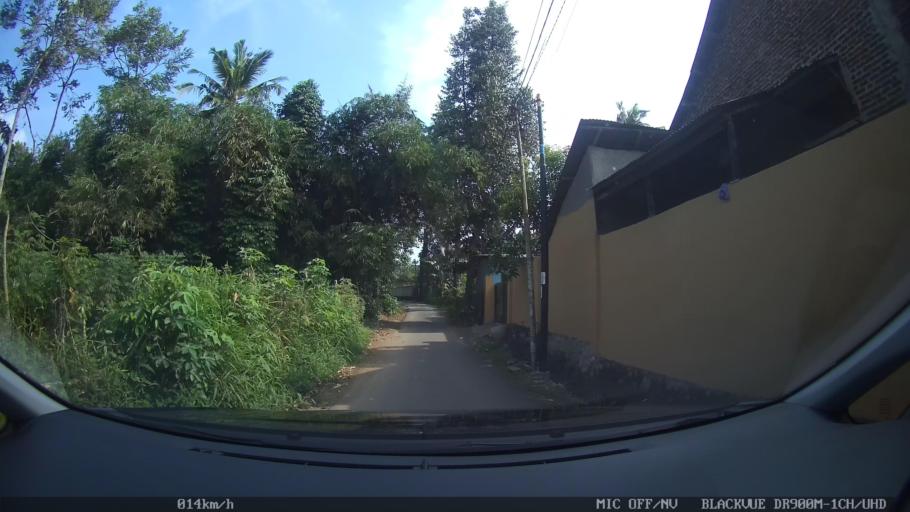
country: ID
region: Lampung
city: Kedaton
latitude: -5.3866
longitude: 105.2234
